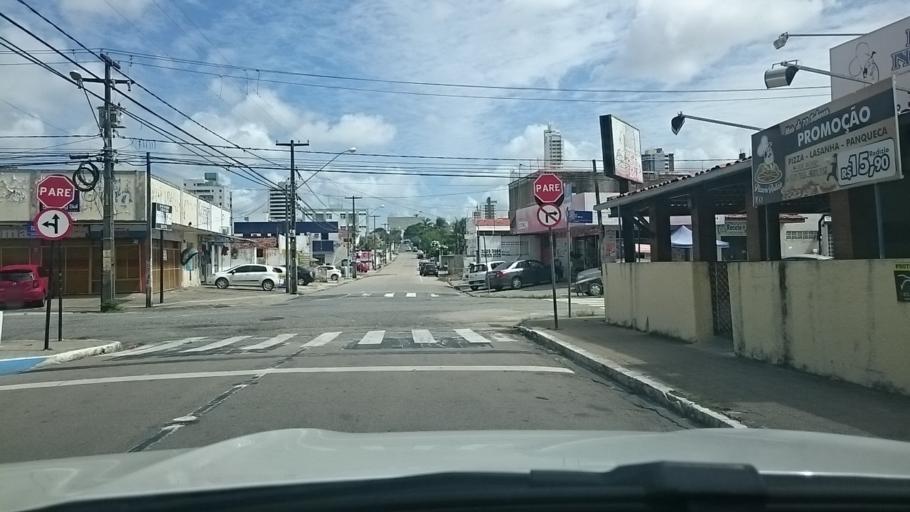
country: BR
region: Paraiba
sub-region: Joao Pessoa
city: Joao Pessoa
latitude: -7.1222
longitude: -34.8365
